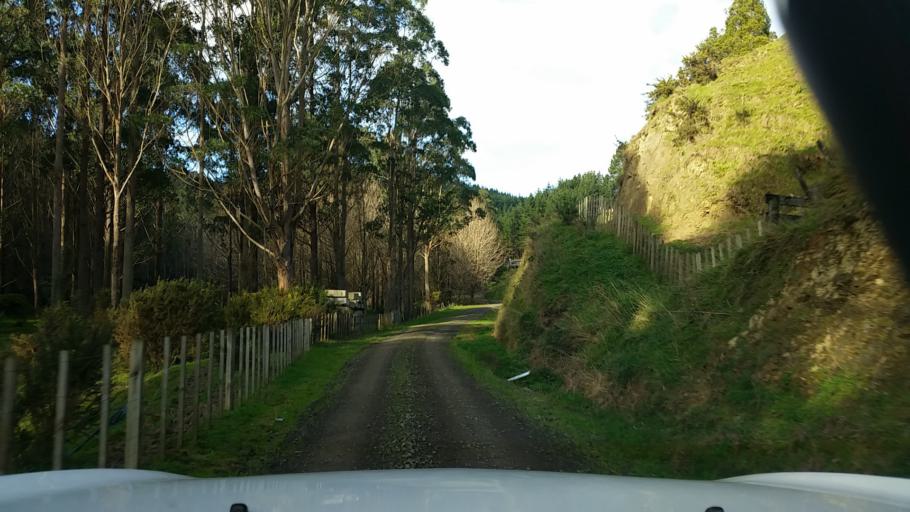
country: NZ
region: Taranaki
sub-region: New Plymouth District
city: Waitara
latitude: -38.9826
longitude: 174.4871
